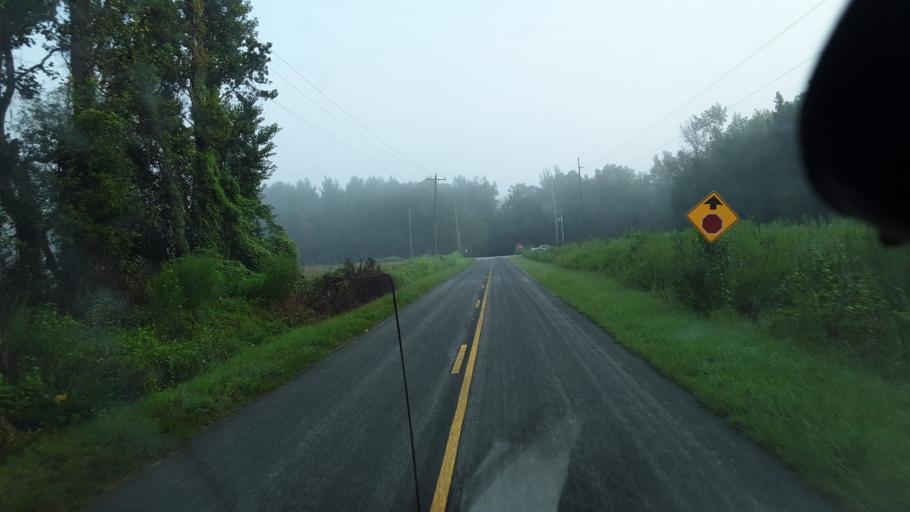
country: US
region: South Carolina
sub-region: Williamsburg County
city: Kingstree
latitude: 33.8219
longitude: -79.9641
